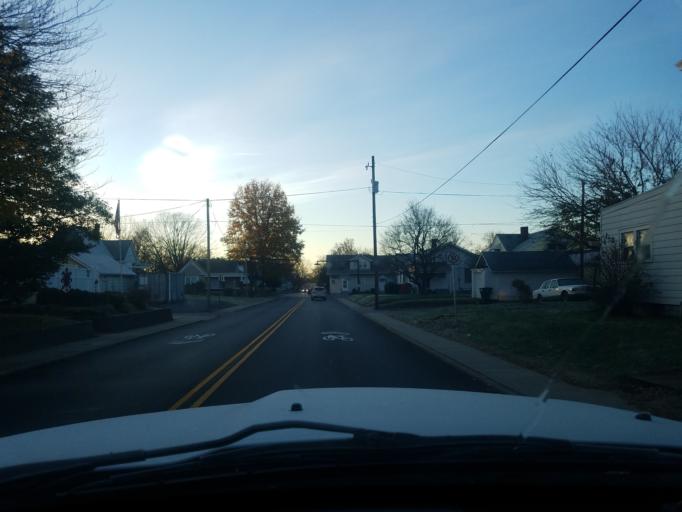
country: US
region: Indiana
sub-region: Floyd County
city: New Albany
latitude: 38.3000
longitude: -85.8031
